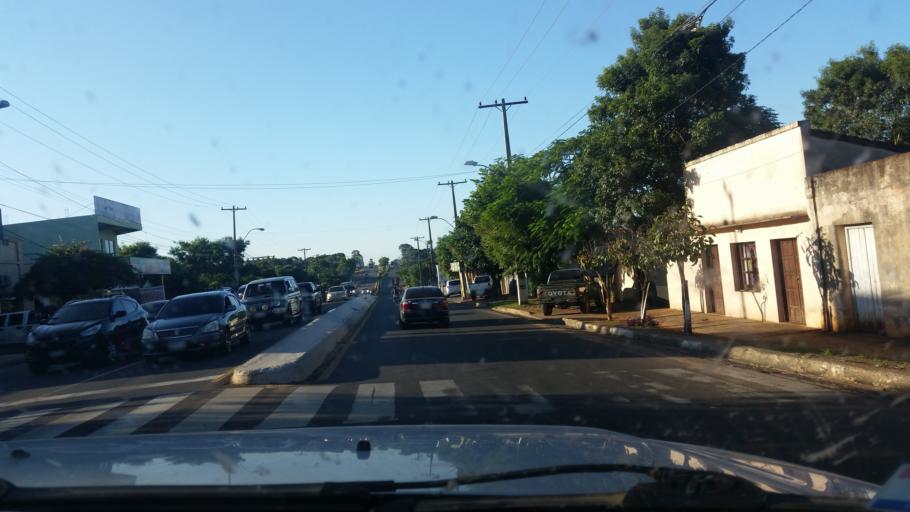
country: PY
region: Misiones
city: Santa Maria
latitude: -26.8847
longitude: -57.0318
